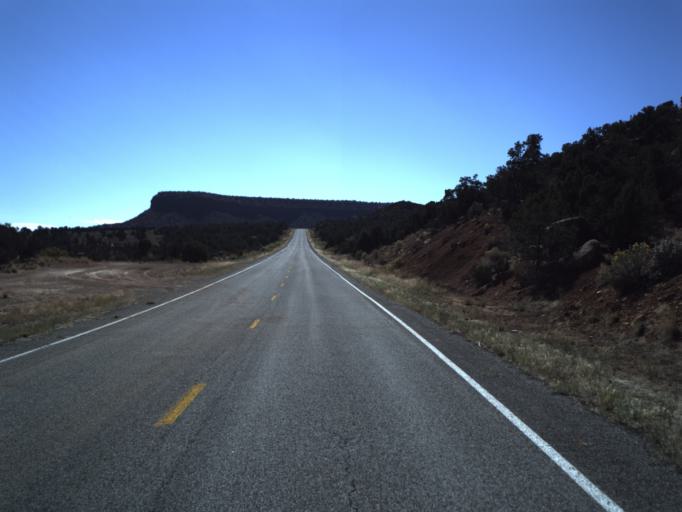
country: US
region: Utah
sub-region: San Juan County
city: Blanding
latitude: 37.5829
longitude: -110.0397
